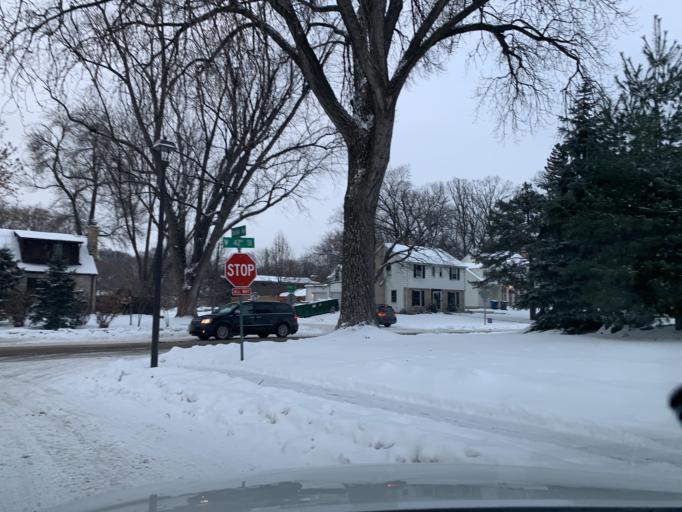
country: US
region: Minnesota
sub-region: Hennepin County
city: Saint Louis Park
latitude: 44.9268
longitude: -93.3387
